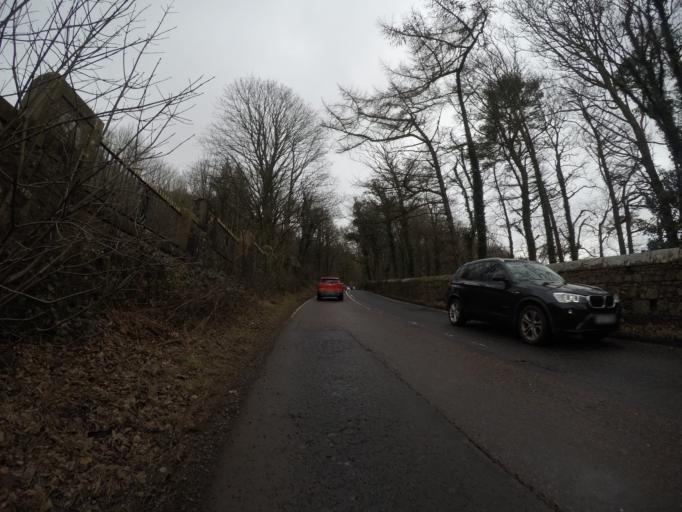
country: GB
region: Scotland
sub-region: North Ayrshire
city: Largs
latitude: 55.7842
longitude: -4.8537
